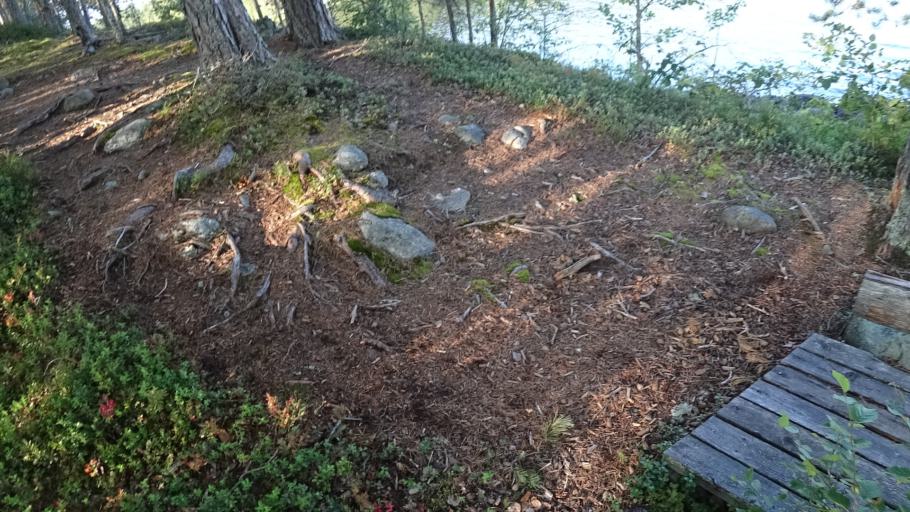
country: FI
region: North Karelia
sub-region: Joensuu
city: Ilomantsi
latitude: 62.5760
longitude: 31.1733
